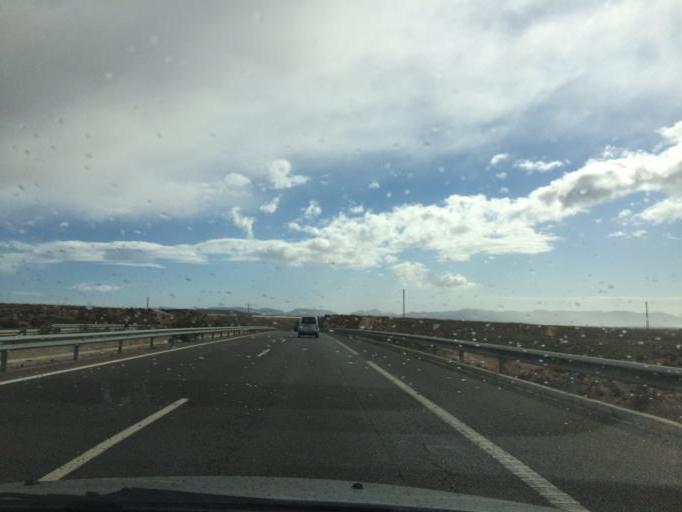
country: ES
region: Andalusia
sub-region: Provincia de Almeria
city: Retamar
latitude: 36.8701
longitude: -2.3243
